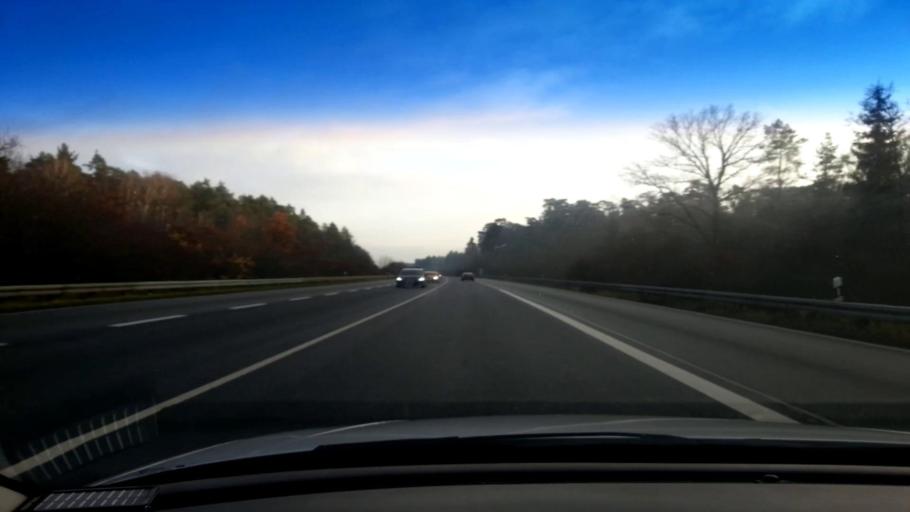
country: DE
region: Bavaria
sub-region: Upper Franconia
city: Strullendorf
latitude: 49.8653
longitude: 10.9476
